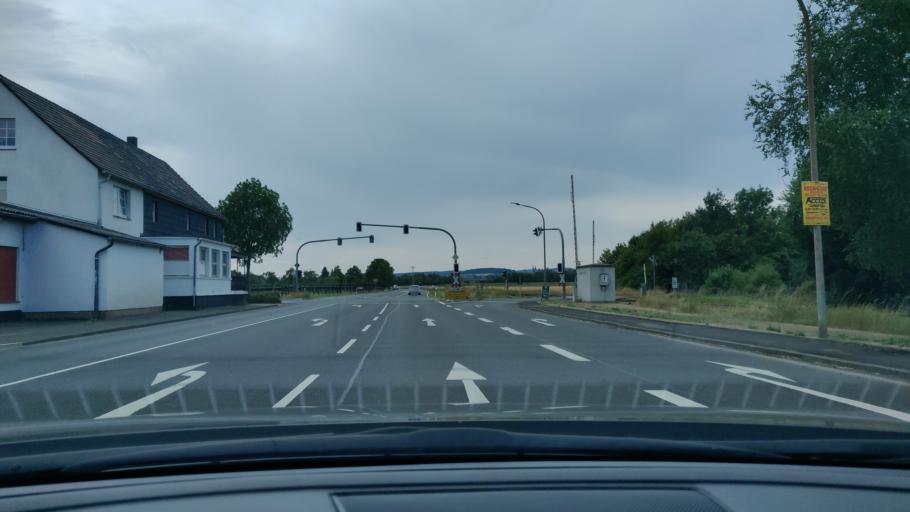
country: DE
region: Hesse
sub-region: Regierungsbezirk Kassel
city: Wabern
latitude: 51.1122
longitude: 9.3163
